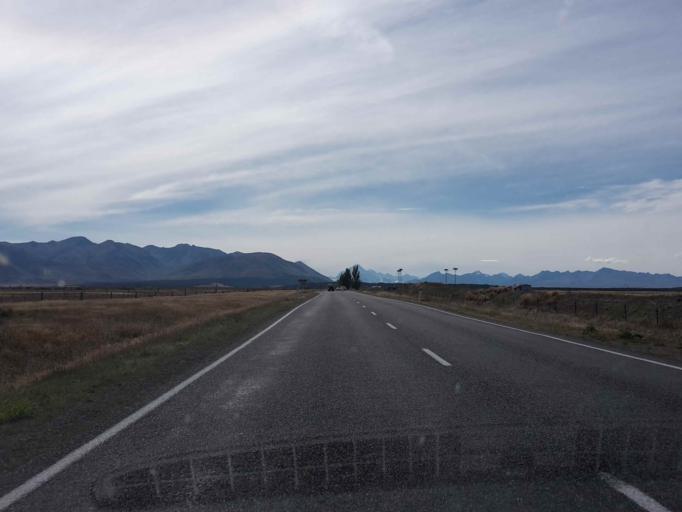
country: NZ
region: Canterbury
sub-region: Timaru District
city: Pleasant Point
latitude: -44.2434
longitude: 170.1164
